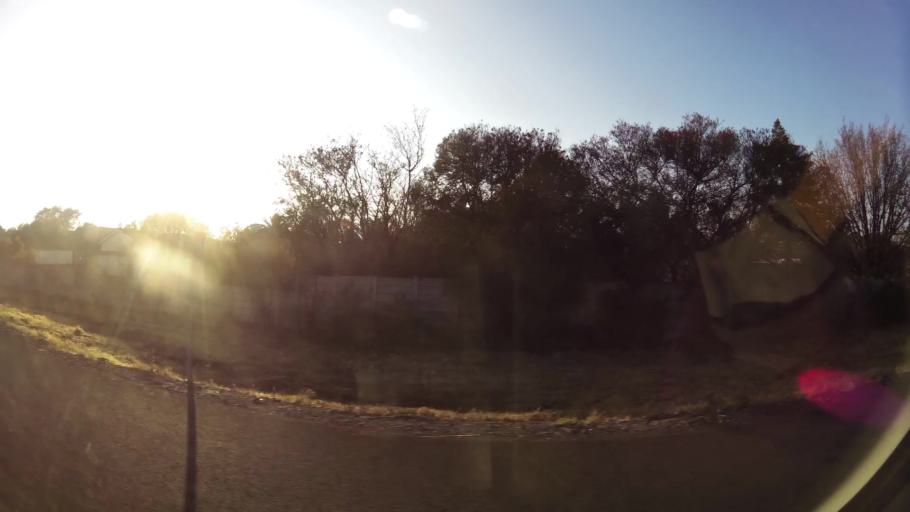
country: ZA
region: Orange Free State
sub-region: Mangaung Metropolitan Municipality
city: Bloemfontein
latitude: -29.1049
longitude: 26.1647
